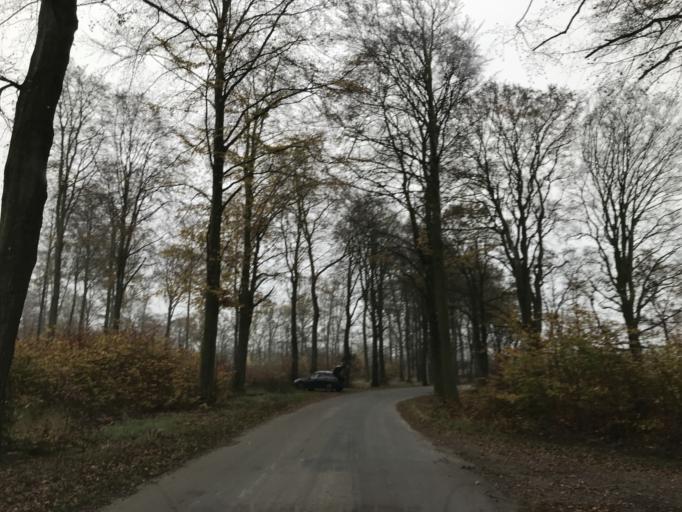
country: SE
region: Skane
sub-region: Klippans Kommun
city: Ljungbyhed
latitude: 55.9841
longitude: 13.1990
